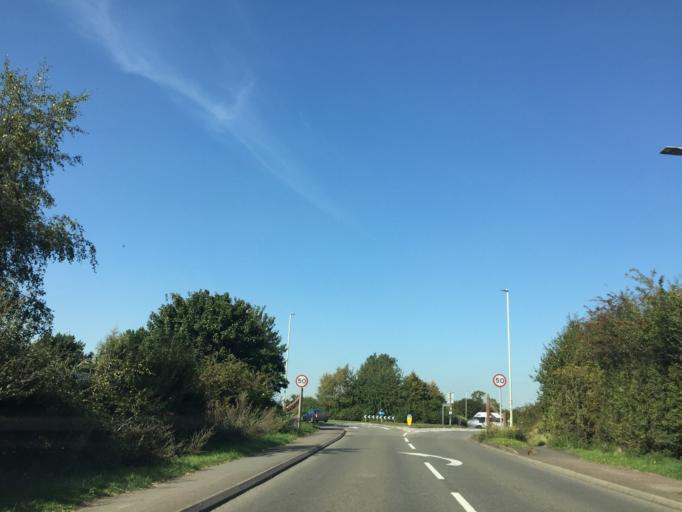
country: GB
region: England
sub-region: Leicestershire
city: Queniborough
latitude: 52.7089
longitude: -1.0504
